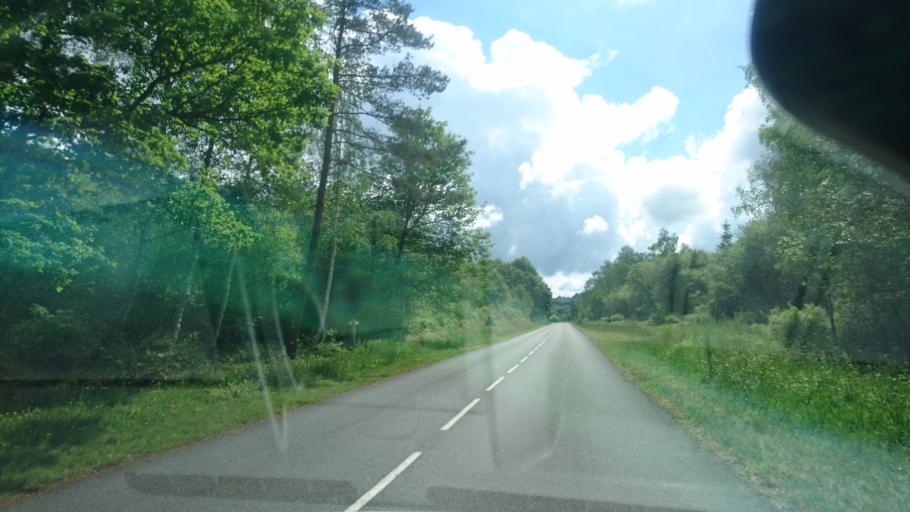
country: FR
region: Limousin
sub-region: Departement de la Haute-Vienne
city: Peyrat-le-Chateau
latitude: 45.7815
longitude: 1.8600
